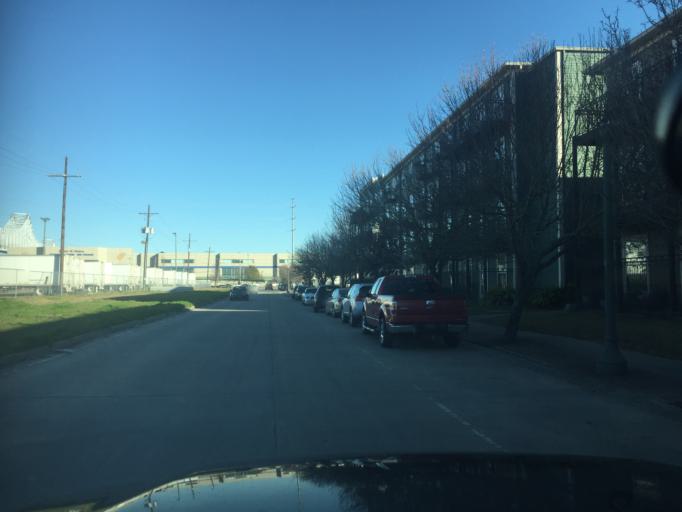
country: US
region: Louisiana
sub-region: Orleans Parish
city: New Orleans
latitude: 29.9367
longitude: -90.0688
